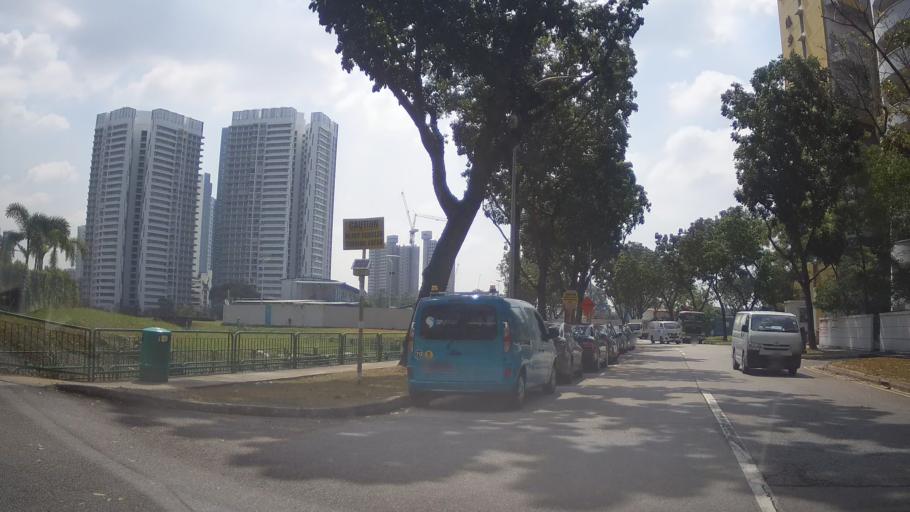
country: SG
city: Singapore
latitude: 1.3122
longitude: 103.8668
